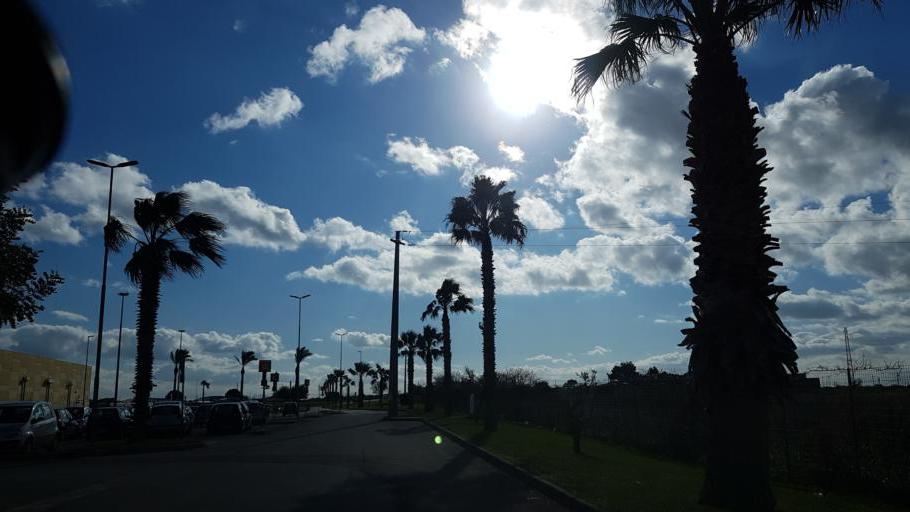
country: IT
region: Apulia
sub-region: Provincia di Brindisi
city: Brindisi
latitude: 40.6183
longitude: 17.9005
